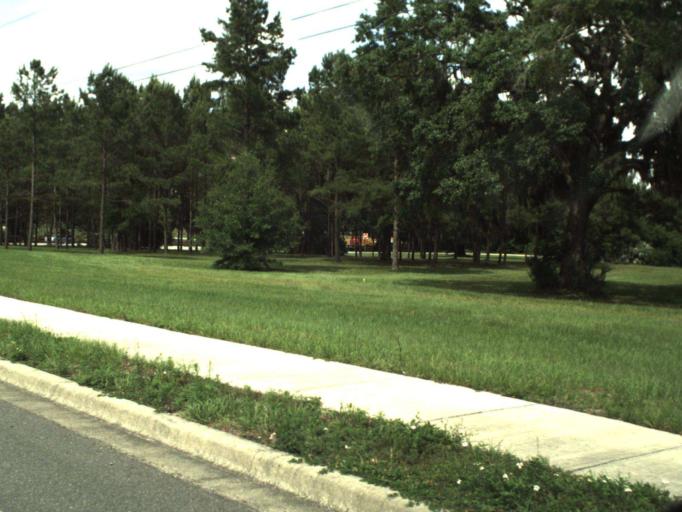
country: US
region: Florida
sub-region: Marion County
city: Silver Springs Shores
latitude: 29.1404
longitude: -82.0535
